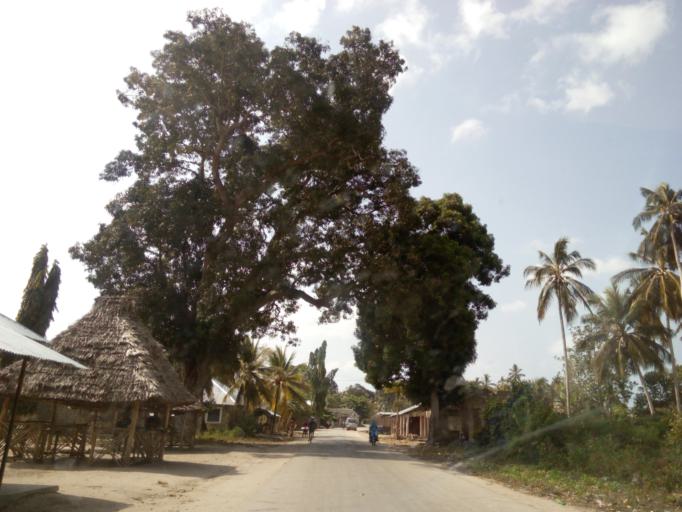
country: TZ
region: Zanzibar Central/South
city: Mahonda
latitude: -6.3064
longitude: 39.3745
